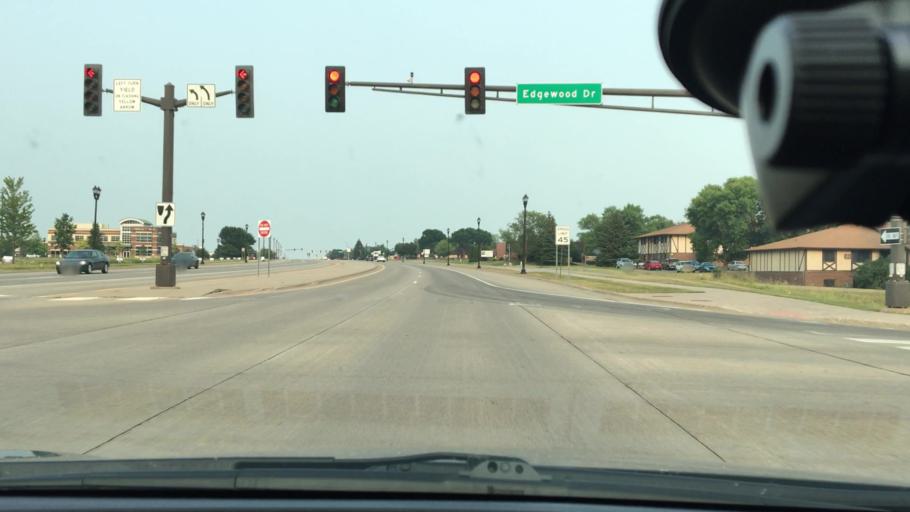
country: US
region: Minnesota
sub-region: Wright County
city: Saint Michael
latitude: 45.2098
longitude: -93.6538
